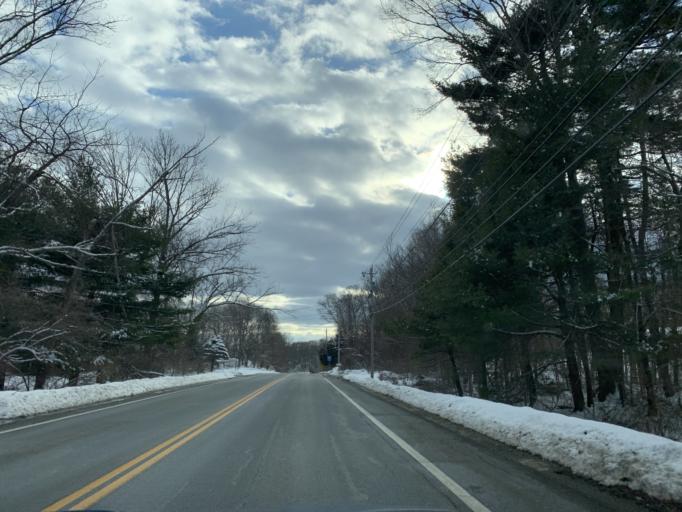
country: US
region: Rhode Island
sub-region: Providence County
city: Cumberland Hill
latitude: 41.9909
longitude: -71.4579
